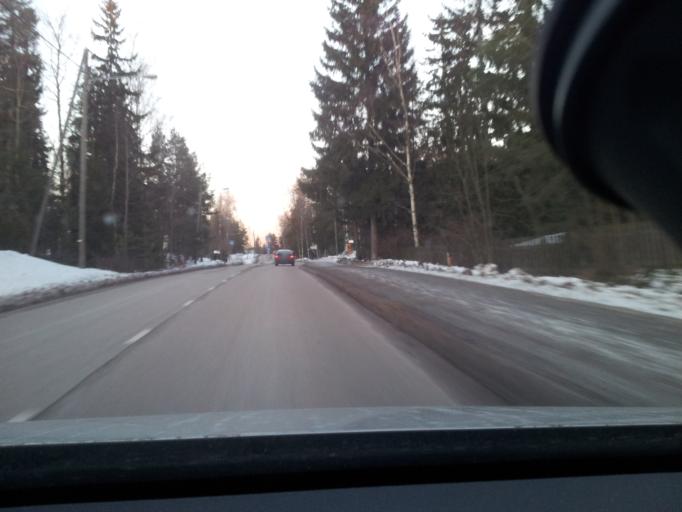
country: FI
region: Uusimaa
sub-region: Helsinki
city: Espoo
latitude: 60.1465
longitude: 24.6814
